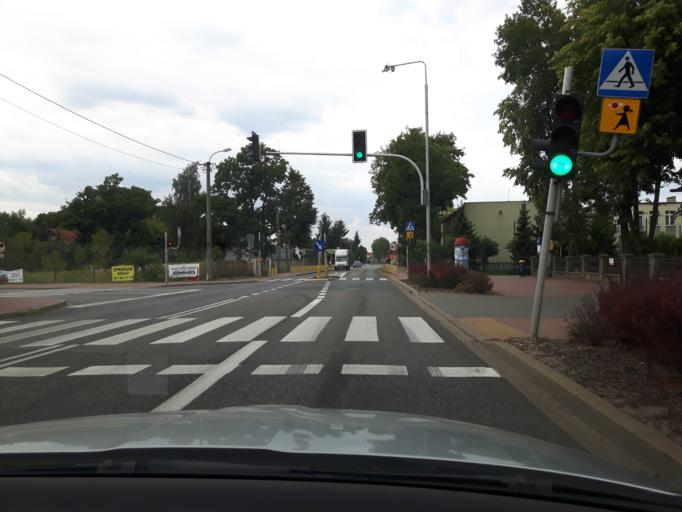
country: PL
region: Masovian Voivodeship
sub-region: Powiat legionowski
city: Wieliszew
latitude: 52.4510
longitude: 20.9695
